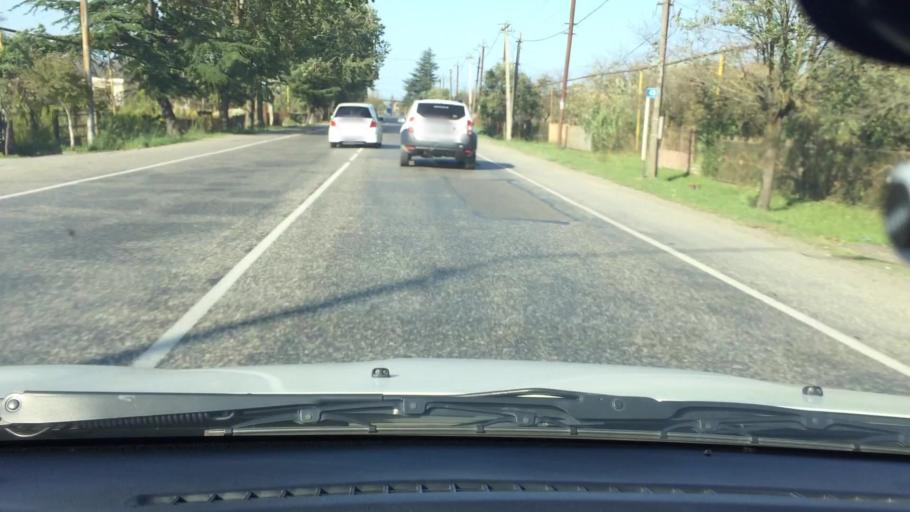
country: GE
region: Imereti
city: Samtredia
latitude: 42.1650
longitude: 42.3720
